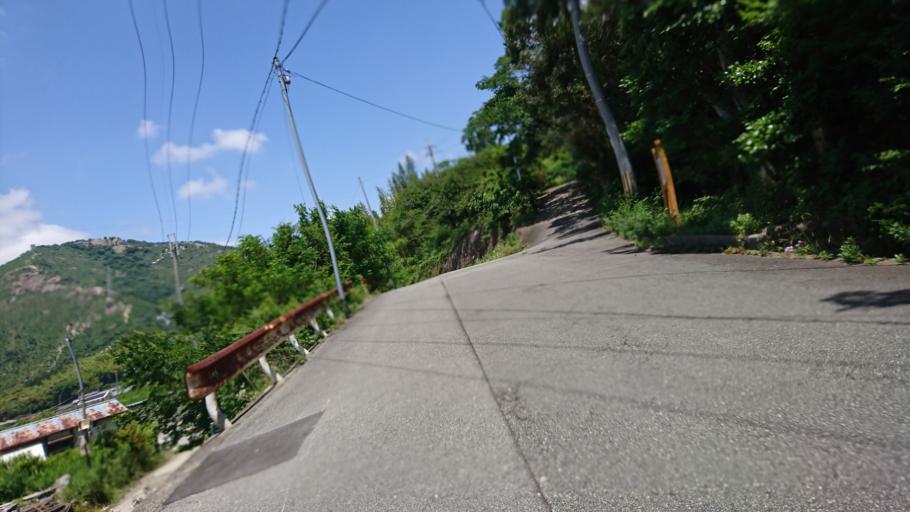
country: JP
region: Hyogo
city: Kakogawacho-honmachi
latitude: 34.8025
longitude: 134.7908
